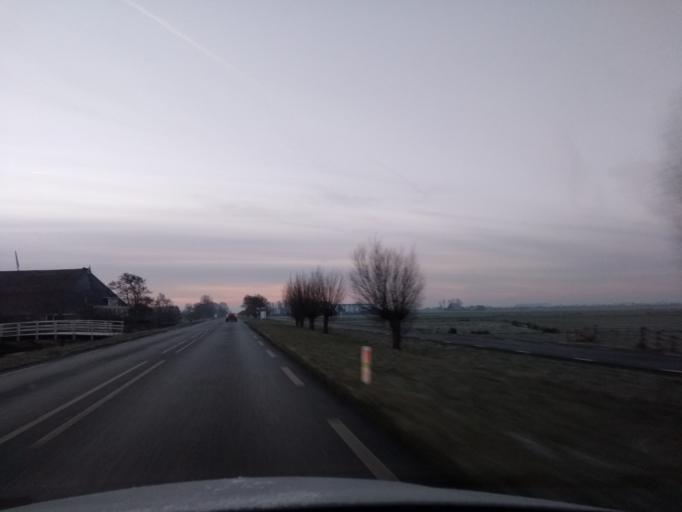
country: NL
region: Friesland
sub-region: Sudwest Fryslan
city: Woudsend
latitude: 52.9581
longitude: 5.6522
